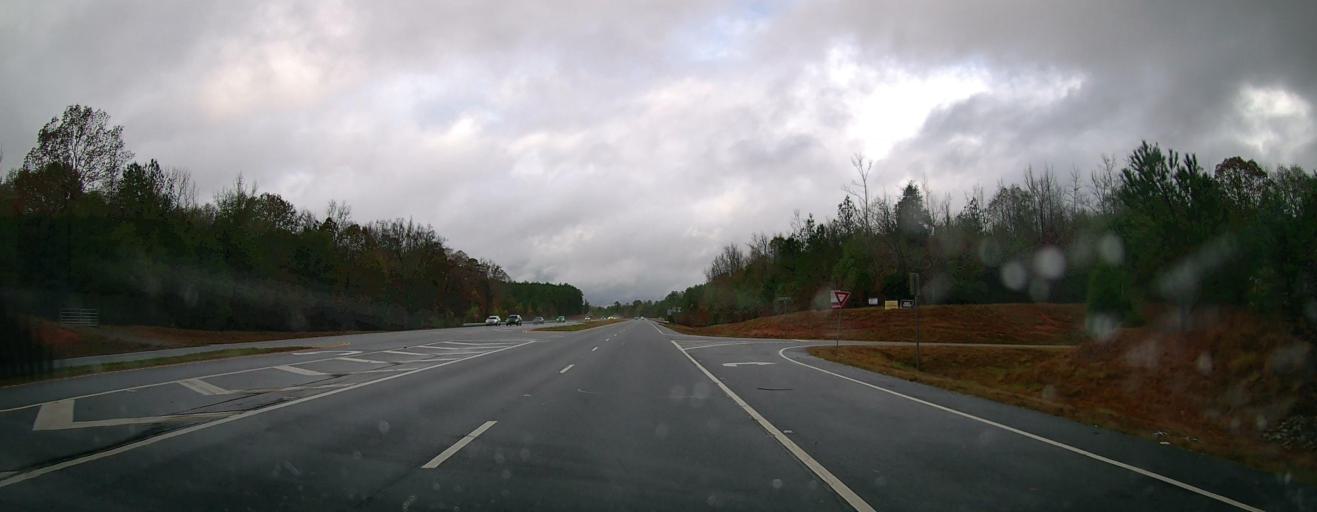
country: US
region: Georgia
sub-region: Jackson County
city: Nicholson
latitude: 34.0694
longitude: -83.4248
